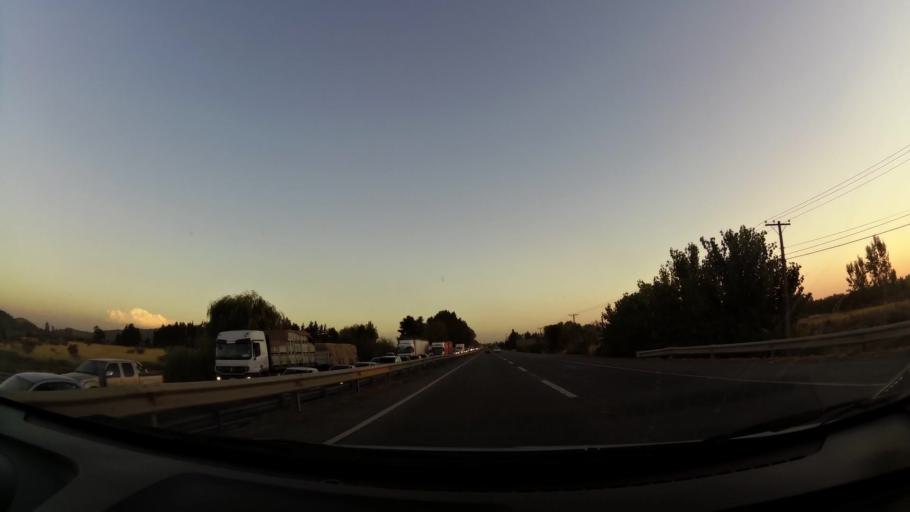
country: CL
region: Maule
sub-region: Provincia de Linares
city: Linares
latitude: -35.7491
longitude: -71.6738
